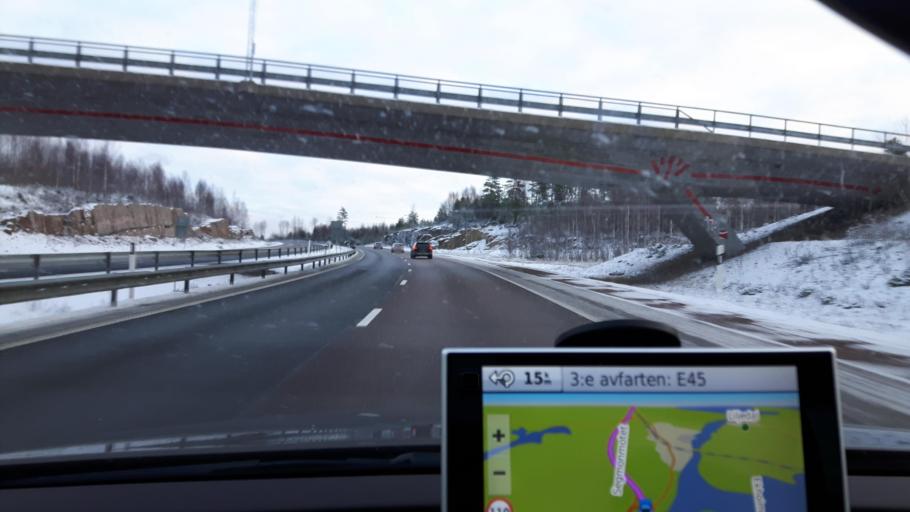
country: SE
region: Vaermland
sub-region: Grums Kommun
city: Slottsbron
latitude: 59.2612
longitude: 13.0035
